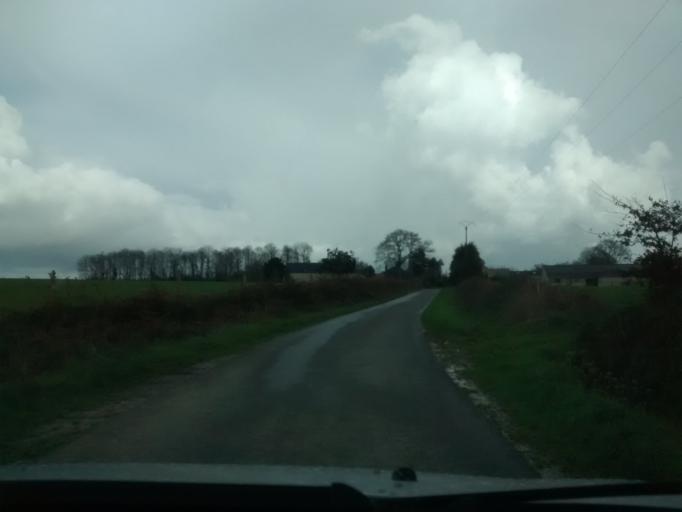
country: FR
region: Brittany
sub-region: Departement d'Ille-et-Vilaine
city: Liffre
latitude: 48.1873
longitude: -1.4994
